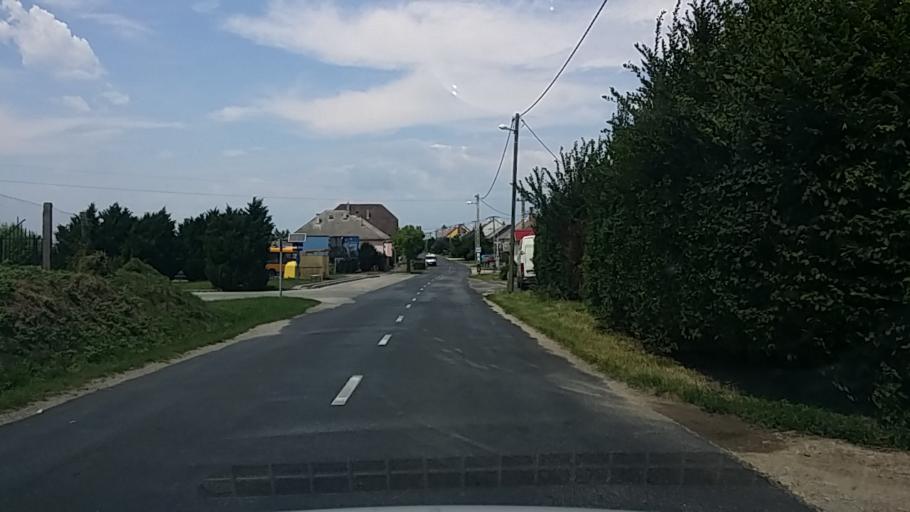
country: HU
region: Zala
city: Nagykanizsa
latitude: 46.4474
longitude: 16.9555
